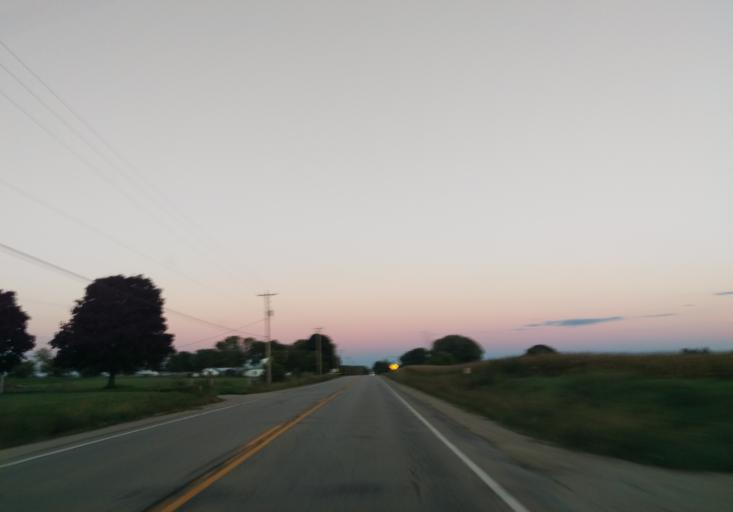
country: US
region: Wisconsin
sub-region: Rock County
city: Janesville
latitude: 42.7304
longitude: -89.0965
